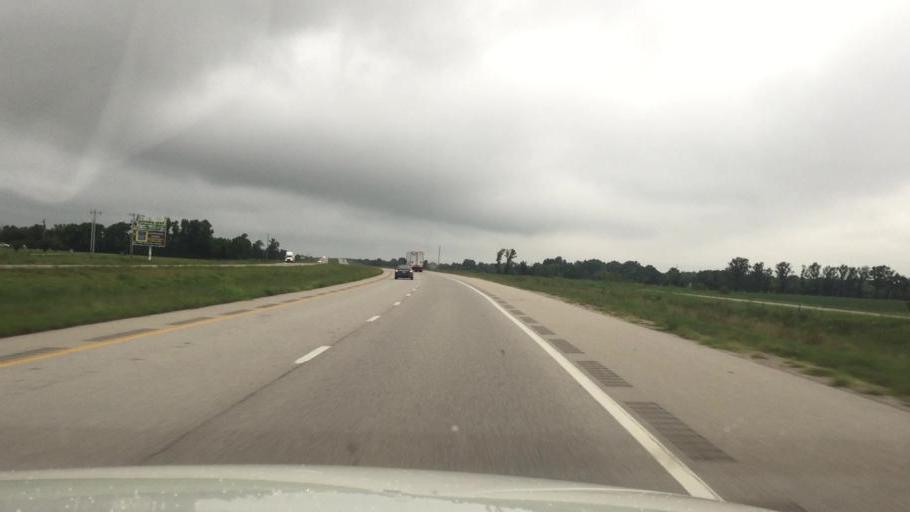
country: US
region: Kansas
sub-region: Montgomery County
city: Coffeyville
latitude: 37.1009
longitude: -95.5895
